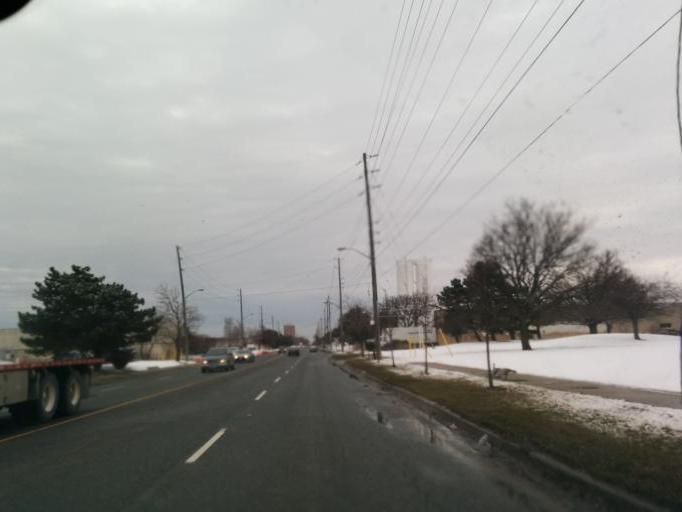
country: CA
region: Ontario
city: Etobicoke
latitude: 43.7425
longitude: -79.6204
